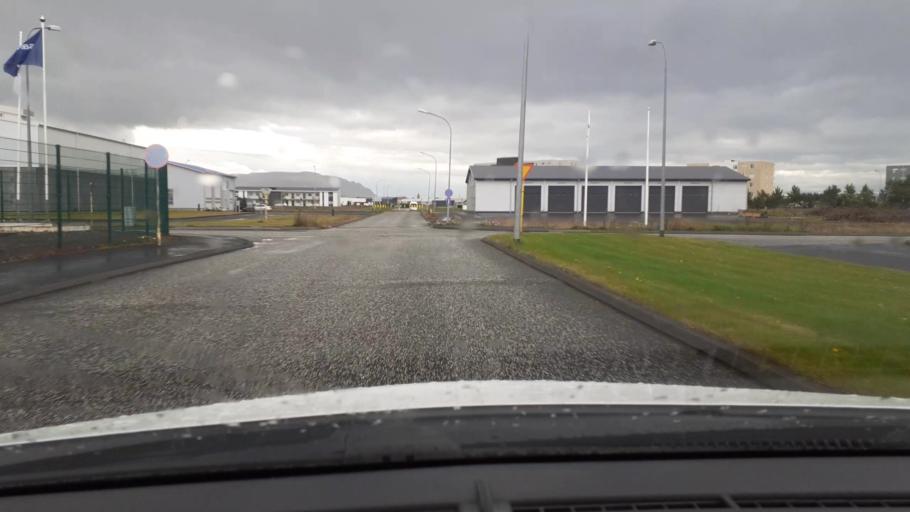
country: IS
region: West
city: Akranes
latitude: 64.3261
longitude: -22.0601
